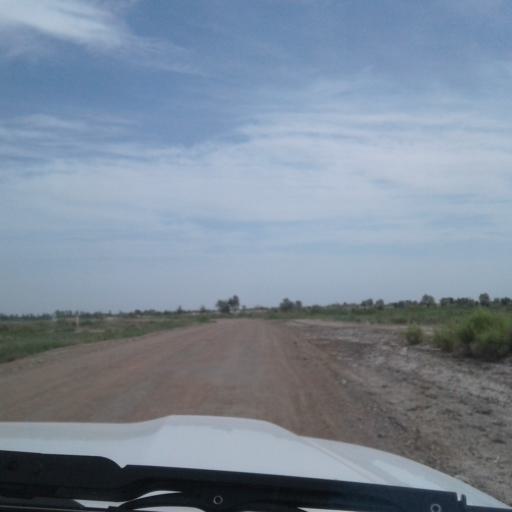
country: TM
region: Dasoguz
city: Tagta
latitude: 41.5518
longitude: 59.8135
